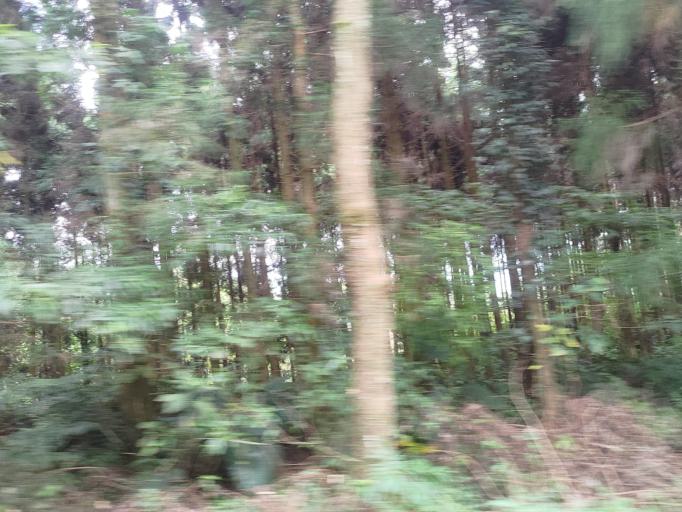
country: TW
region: Taiwan
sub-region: Hsinchu
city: Hsinchu
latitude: 24.6275
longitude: 121.0868
